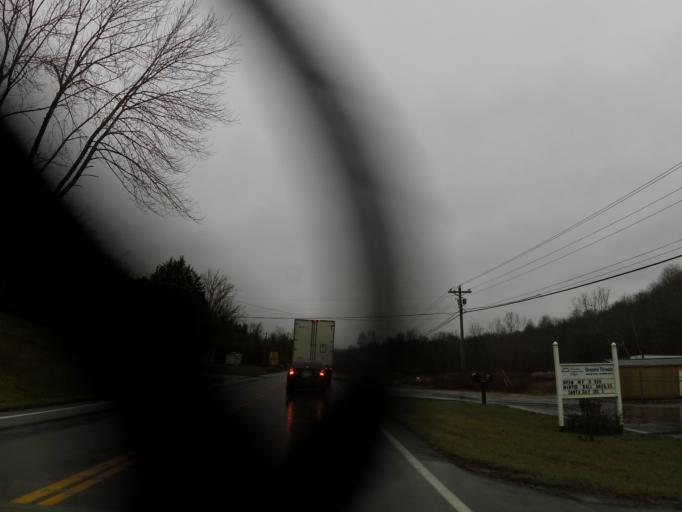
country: US
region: Kentucky
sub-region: Rockcastle County
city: Mount Vernon
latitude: 37.3968
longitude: -84.3341
